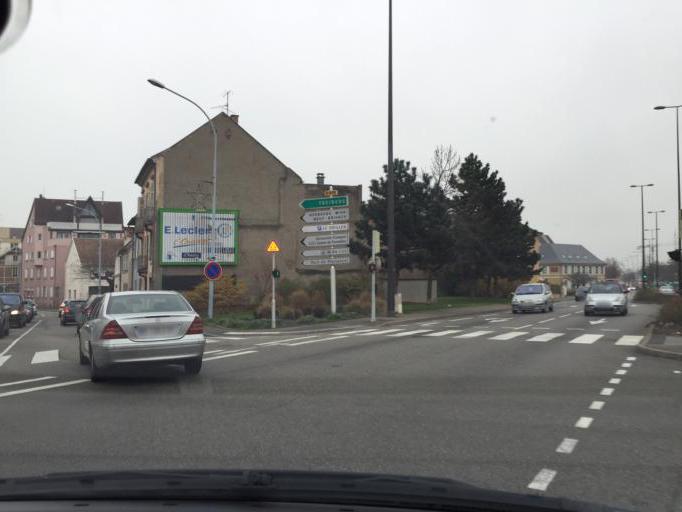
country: FR
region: Alsace
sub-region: Departement du Haut-Rhin
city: Colmar
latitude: 48.0802
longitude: 7.3645
